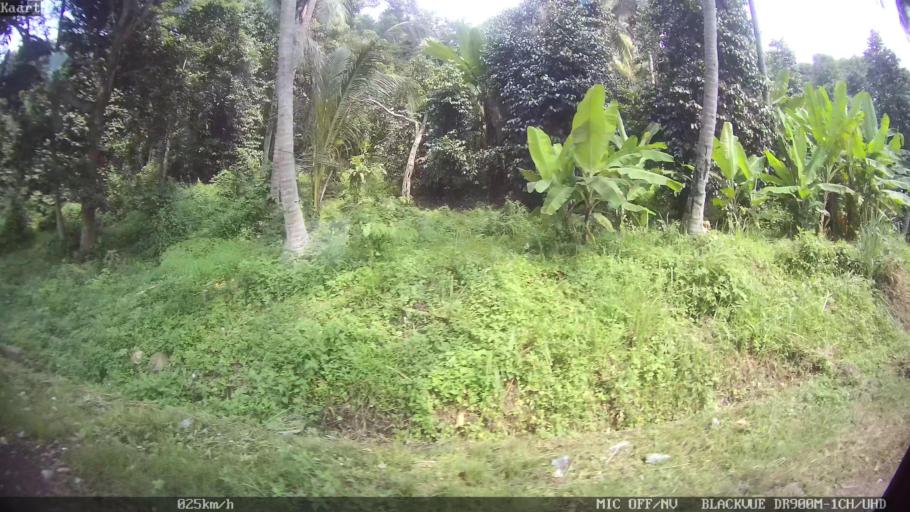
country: ID
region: Lampung
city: Bandarlampung
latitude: -5.4590
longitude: 105.2442
